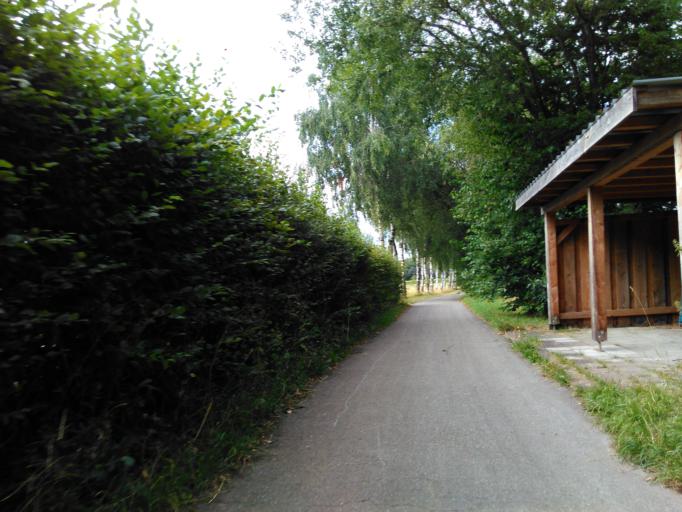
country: LU
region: Grevenmacher
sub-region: Canton d'Echternach
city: Consdorf
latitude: 49.7653
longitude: 6.3432
